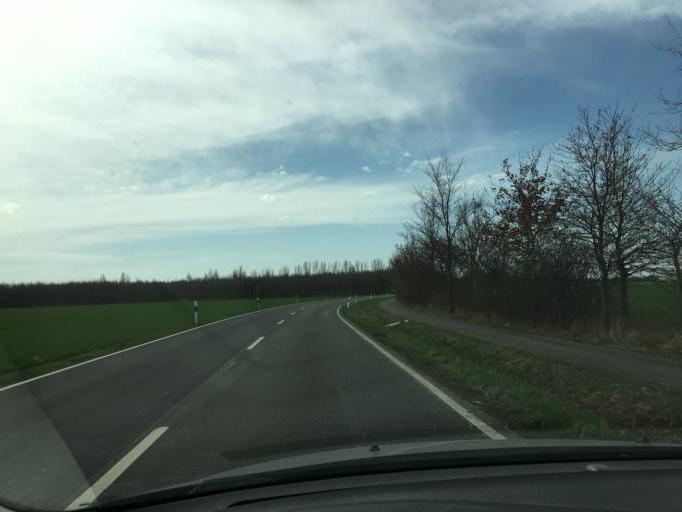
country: DE
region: Saxony
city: Taucha
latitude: 51.3625
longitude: 12.4920
